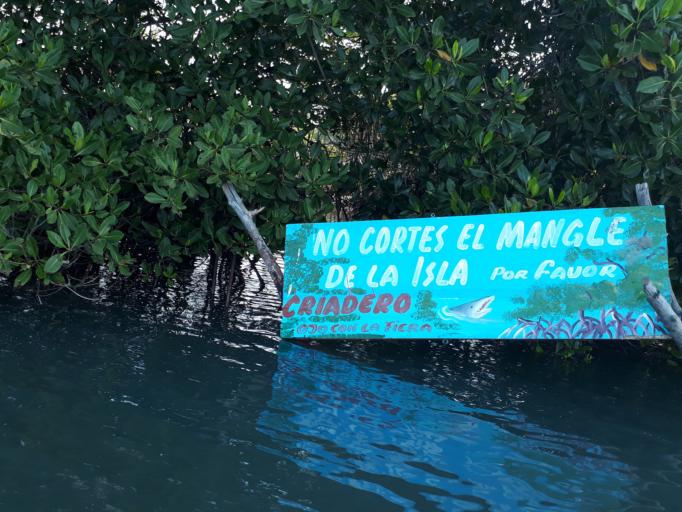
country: CO
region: Bolivar
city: Cartagena
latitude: 10.4848
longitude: -75.4825
